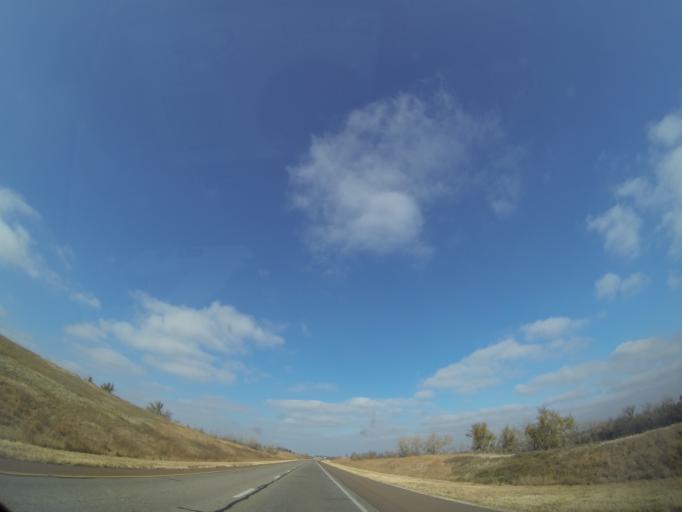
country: US
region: Kansas
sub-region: McPherson County
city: Lindsborg
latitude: 38.4957
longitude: -97.6194
